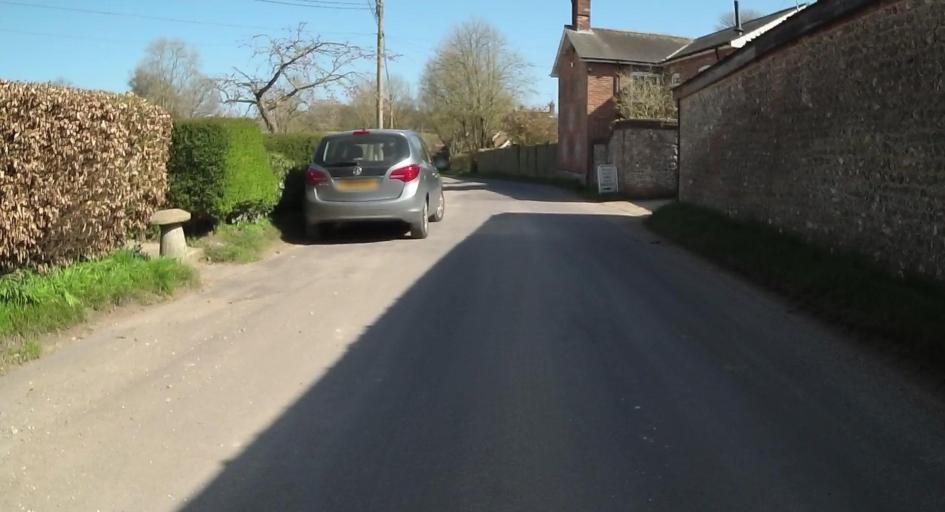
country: GB
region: England
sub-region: Hampshire
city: Highclere
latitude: 51.2787
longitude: -1.4012
